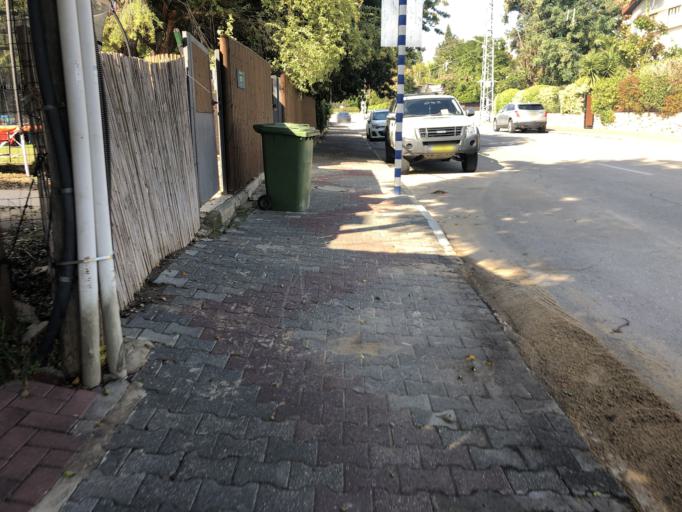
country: IL
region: Tel Aviv
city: Or Yehuda
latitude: 32.0314
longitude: 34.8735
